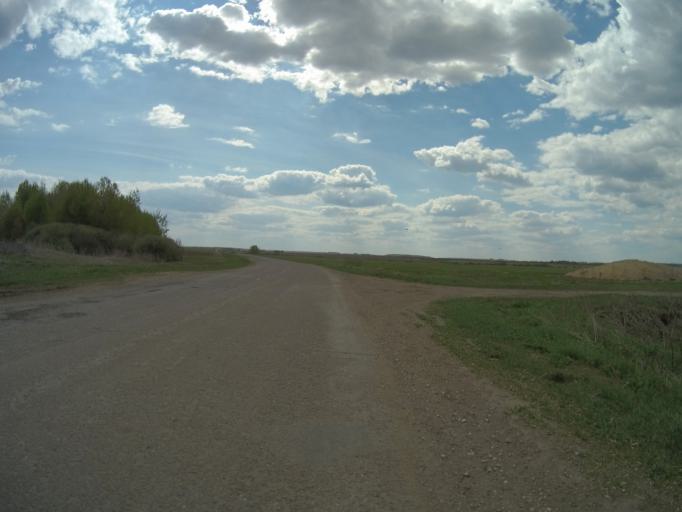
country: RU
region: Vladimir
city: Suzdal'
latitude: 56.3241
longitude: 40.2994
